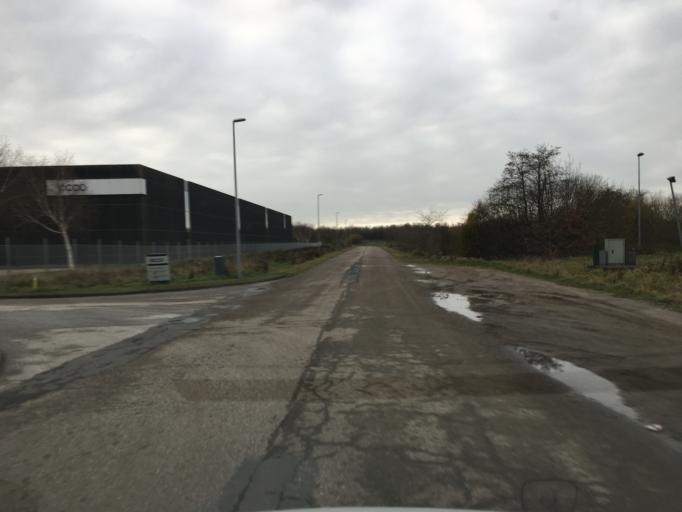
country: DK
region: South Denmark
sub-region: Tonder Kommune
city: Tonder
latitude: 54.9523
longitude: 8.8600
